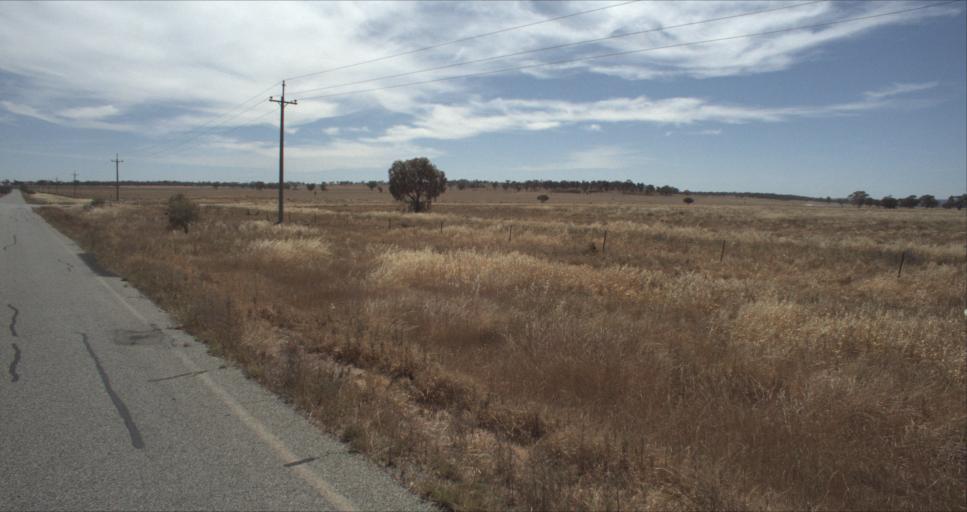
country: AU
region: New South Wales
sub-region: Leeton
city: Leeton
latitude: -34.6306
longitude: 146.4560
